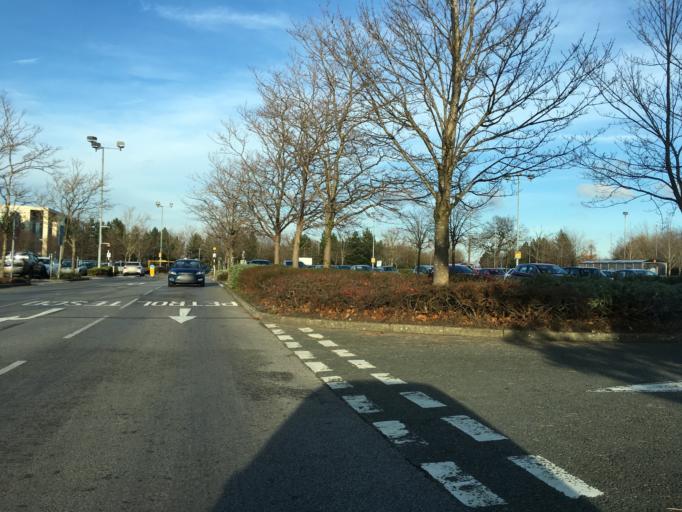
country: GB
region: England
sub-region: Borough of Stockport
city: Cheadle Hulme
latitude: 53.3498
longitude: -2.2035
